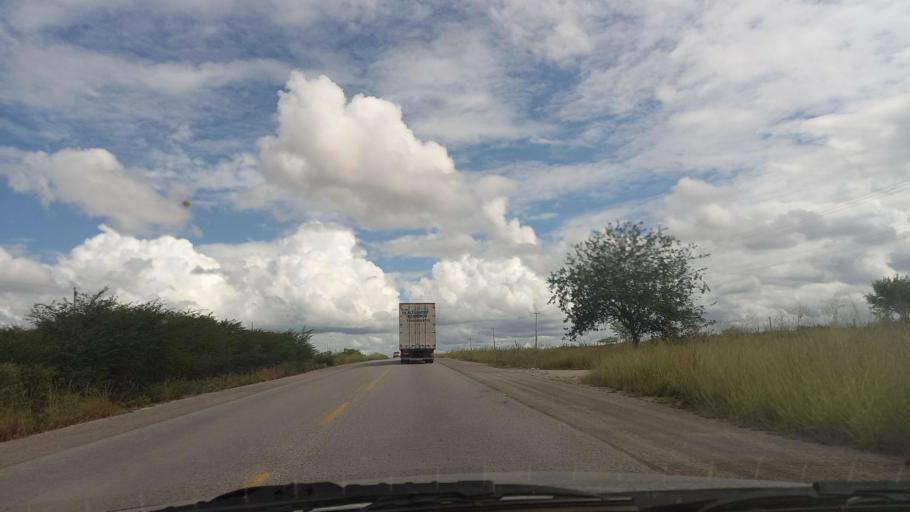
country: BR
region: Pernambuco
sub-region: Cachoeirinha
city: Cachoeirinha
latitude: -8.4160
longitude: -36.1919
